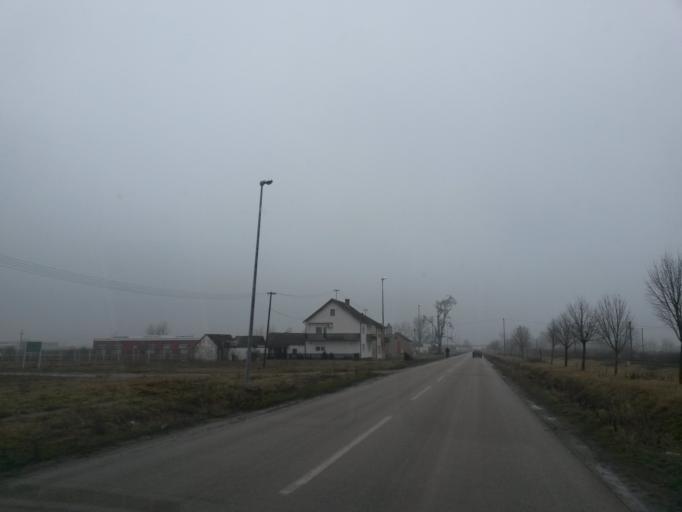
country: HR
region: Vukovarsko-Srijemska
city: Zupanja
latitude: 45.0977
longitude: 18.6980
